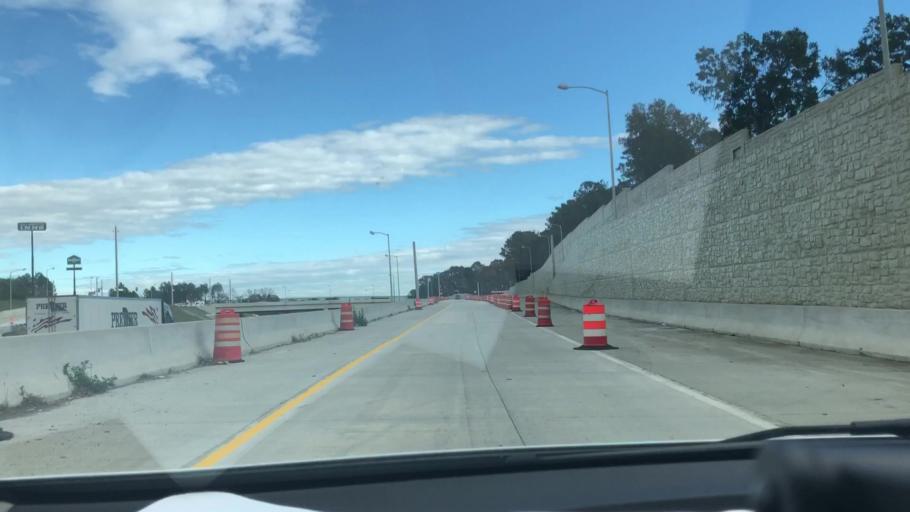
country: US
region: Georgia
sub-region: DeKalb County
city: Panthersville
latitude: 33.6987
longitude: -84.2696
